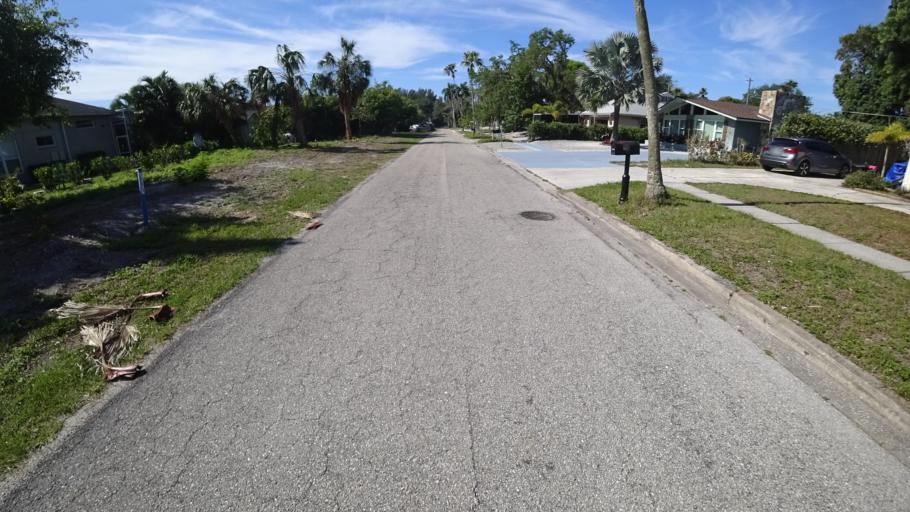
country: US
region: Florida
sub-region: Manatee County
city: West Bradenton
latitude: 27.5064
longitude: -82.6447
